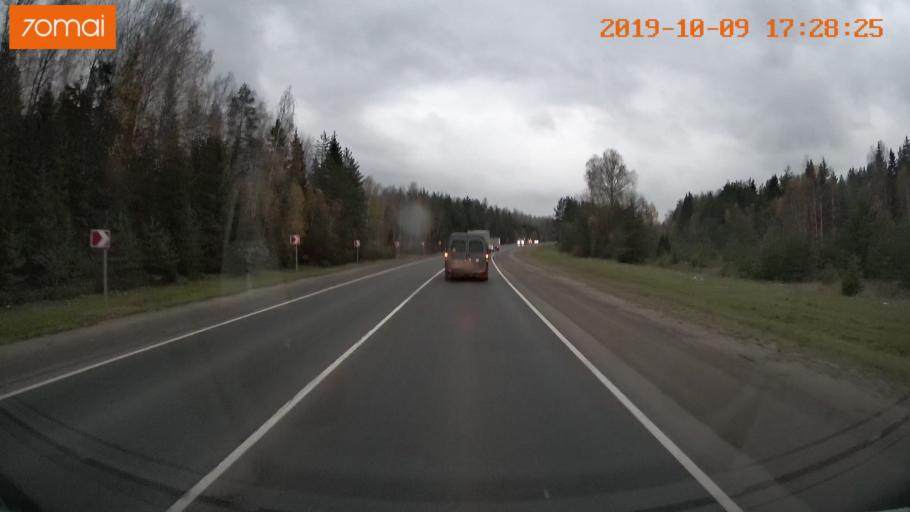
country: RU
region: Ivanovo
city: Furmanov
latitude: 57.1581
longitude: 41.0684
